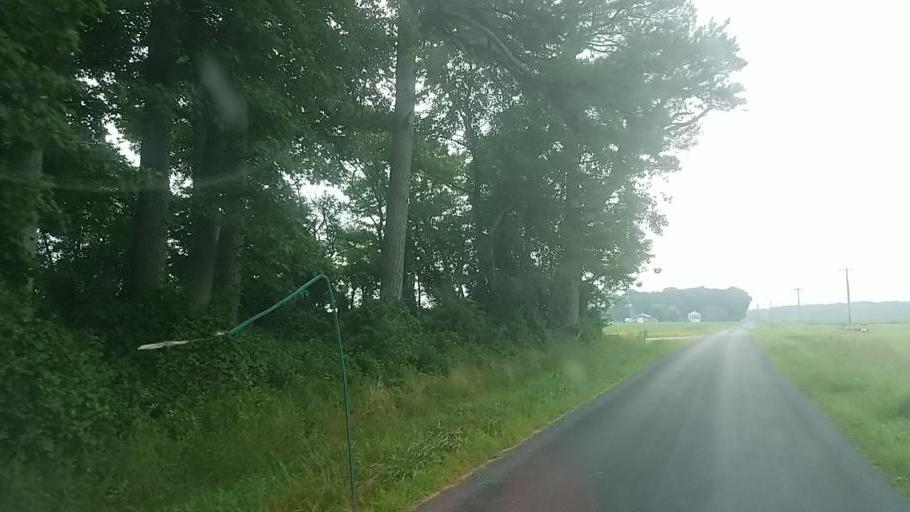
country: US
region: Delaware
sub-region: Sussex County
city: Selbyville
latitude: 38.4434
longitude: -75.2680
